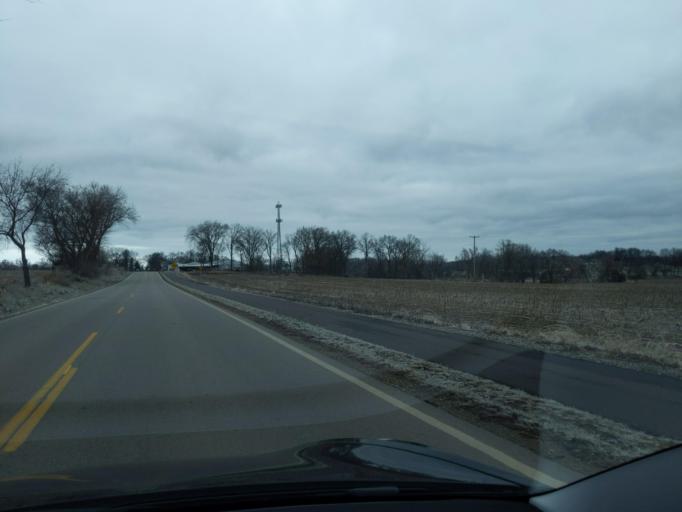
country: US
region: Michigan
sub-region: Jackson County
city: Spring Arbor
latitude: 42.1928
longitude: -84.5534
